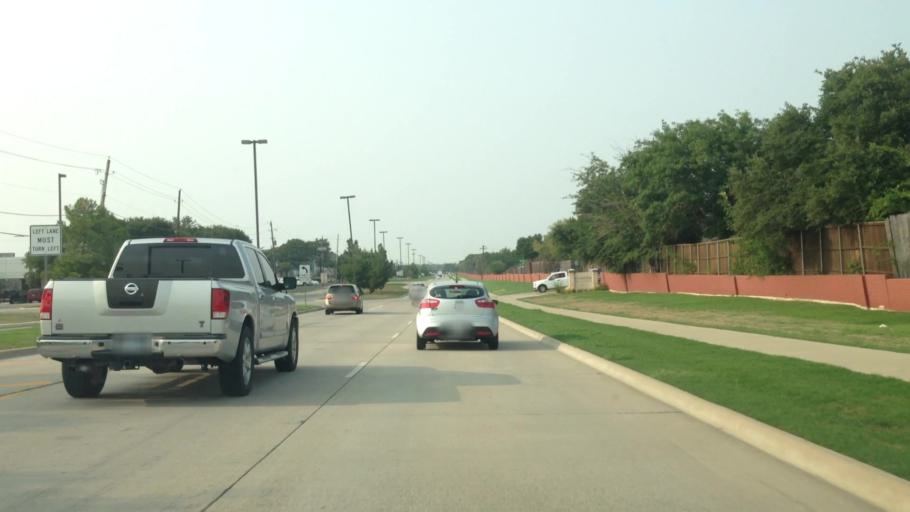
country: US
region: Texas
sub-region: Dallas County
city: Carrollton
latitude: 32.9870
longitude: -96.9201
